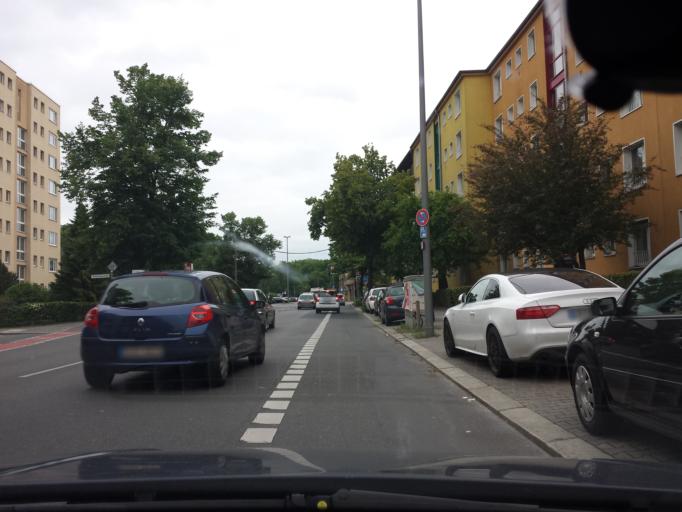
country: DE
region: Berlin
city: Spandau
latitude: 52.5438
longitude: 13.2067
